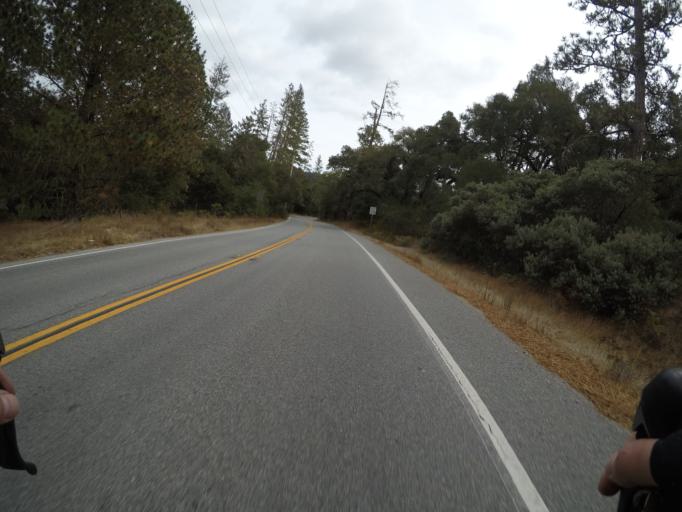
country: US
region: California
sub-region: Santa Cruz County
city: Ben Lomond
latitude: 37.0801
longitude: -122.0624
